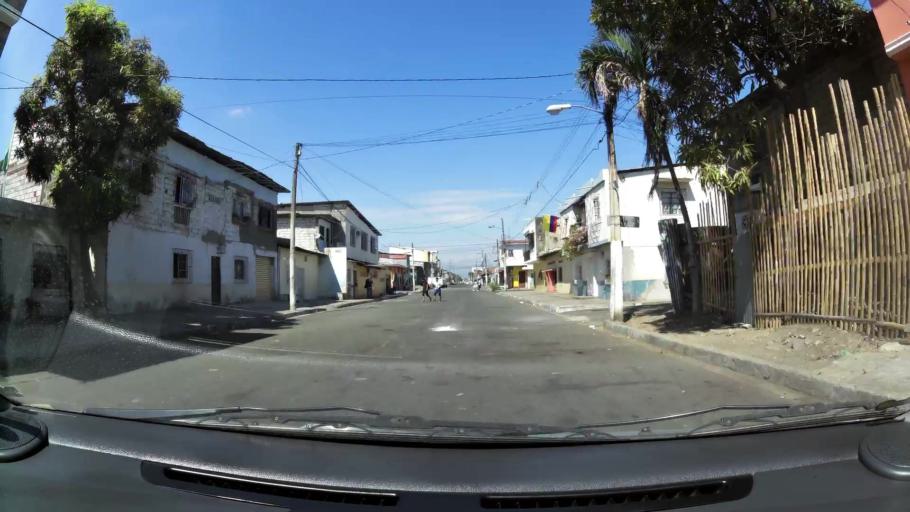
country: EC
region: Guayas
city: Guayaquil
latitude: -2.2041
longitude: -79.9357
